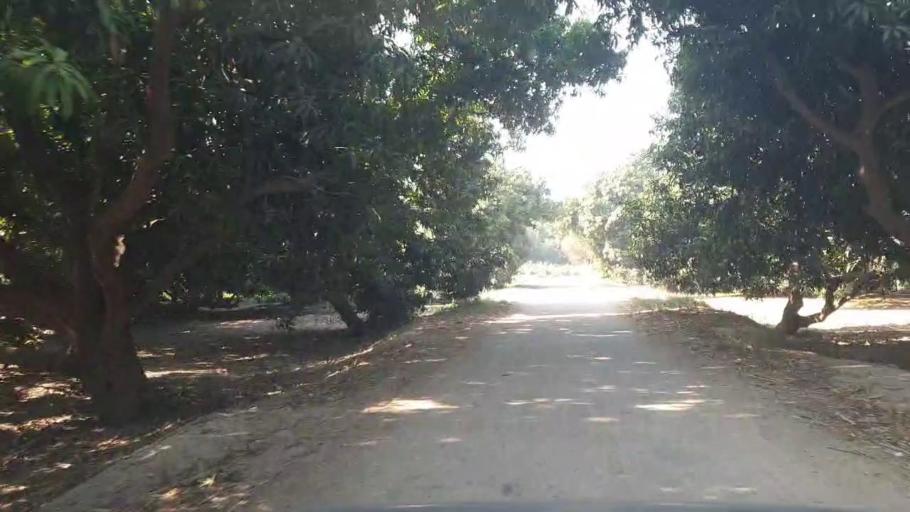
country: PK
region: Sindh
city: Tando Allahyar
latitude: 25.4667
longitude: 68.7633
